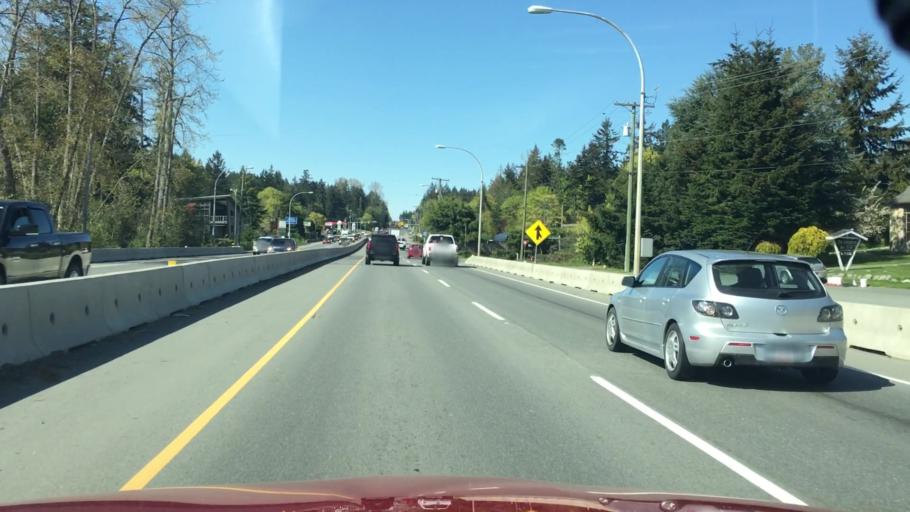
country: CA
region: British Columbia
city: Victoria
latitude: 48.5329
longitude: -123.3882
